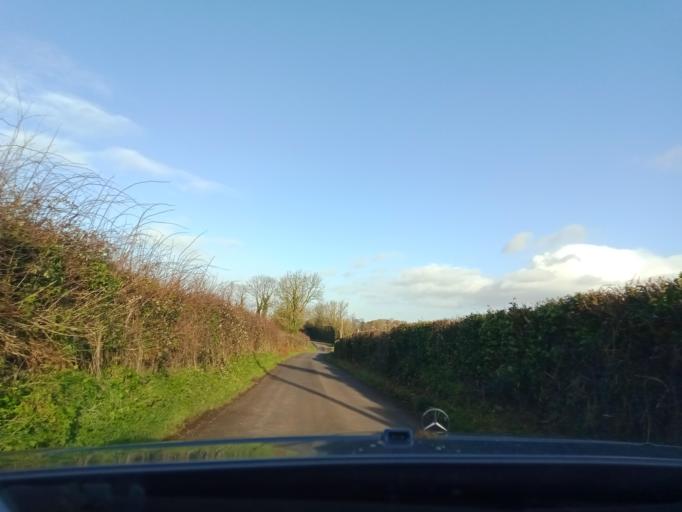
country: IE
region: Leinster
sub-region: Kilkenny
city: Callan
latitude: 52.4990
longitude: -7.3551
